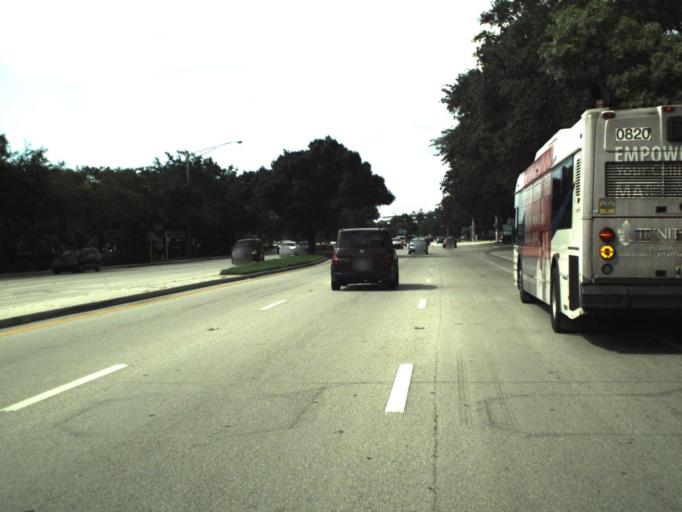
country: US
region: Florida
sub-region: Broward County
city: Tamarac
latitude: 26.2407
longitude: -80.2542
